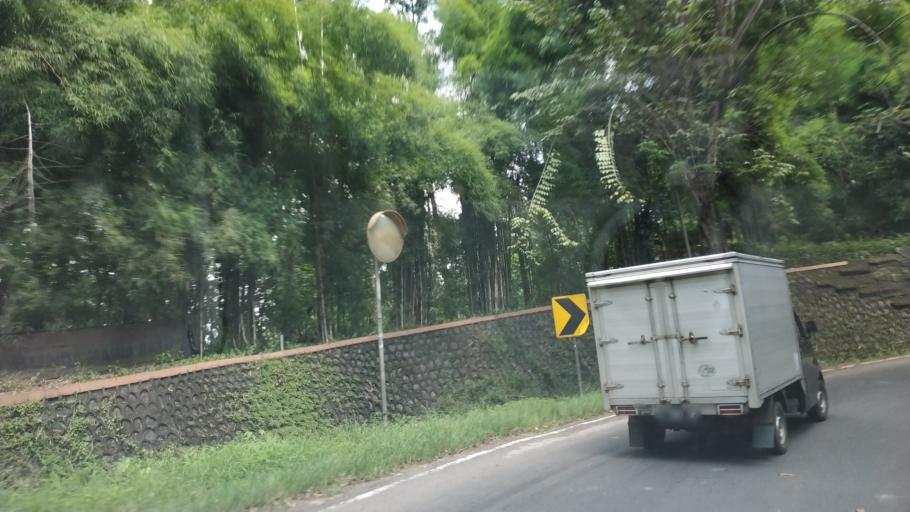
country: ID
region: Central Java
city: Weleri
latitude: -7.0030
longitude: 110.0662
